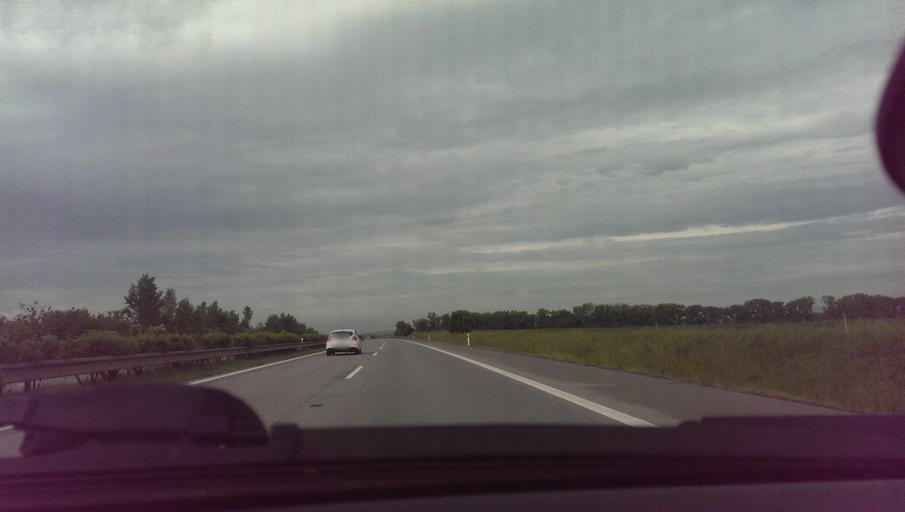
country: CZ
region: South Moravian
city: Ivanovice na Hane
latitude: 49.3025
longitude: 17.1165
